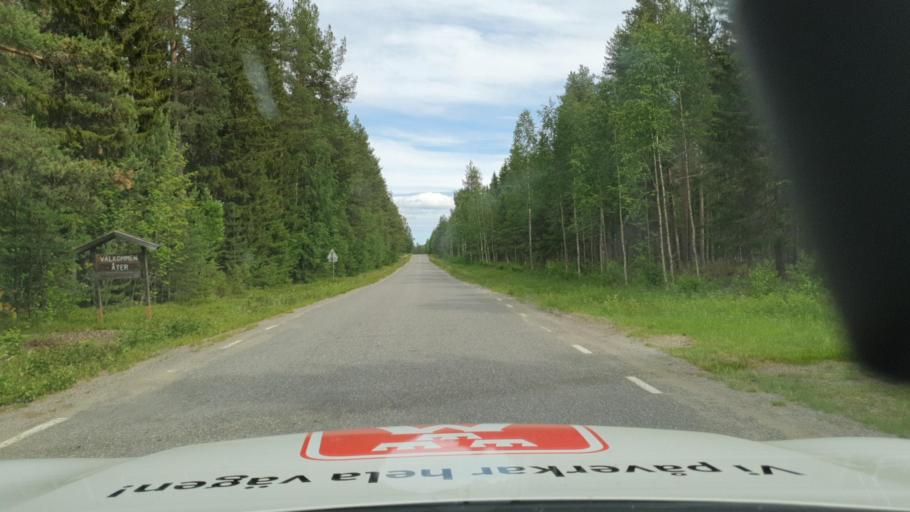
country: SE
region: Vaesterbotten
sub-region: Skelleftea Kommun
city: Viken
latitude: 64.4983
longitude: 20.8814
